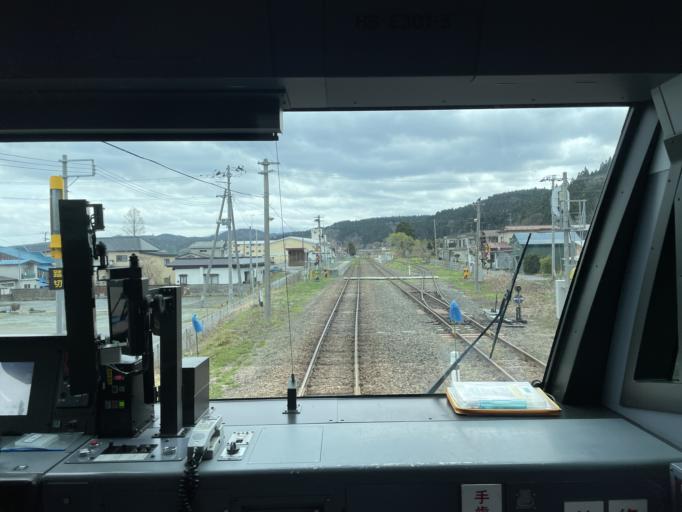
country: JP
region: Aomori
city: Shimokizukuri
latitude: 40.7467
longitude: 140.0941
